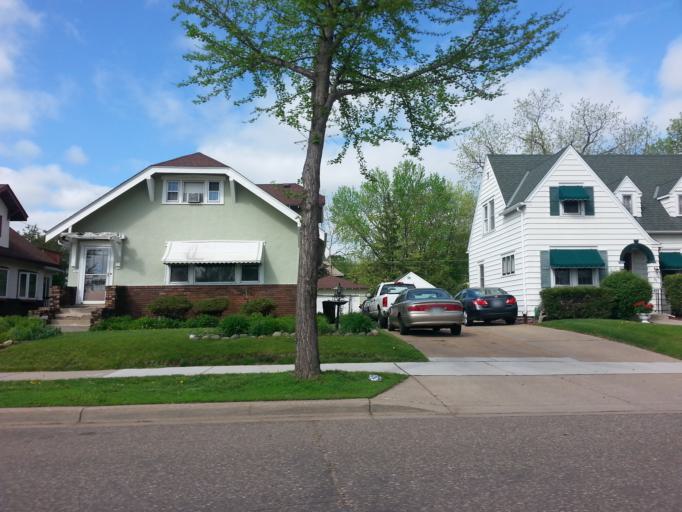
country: US
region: Minnesota
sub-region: Ramsey County
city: Saint Paul
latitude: 44.9481
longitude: -93.0652
